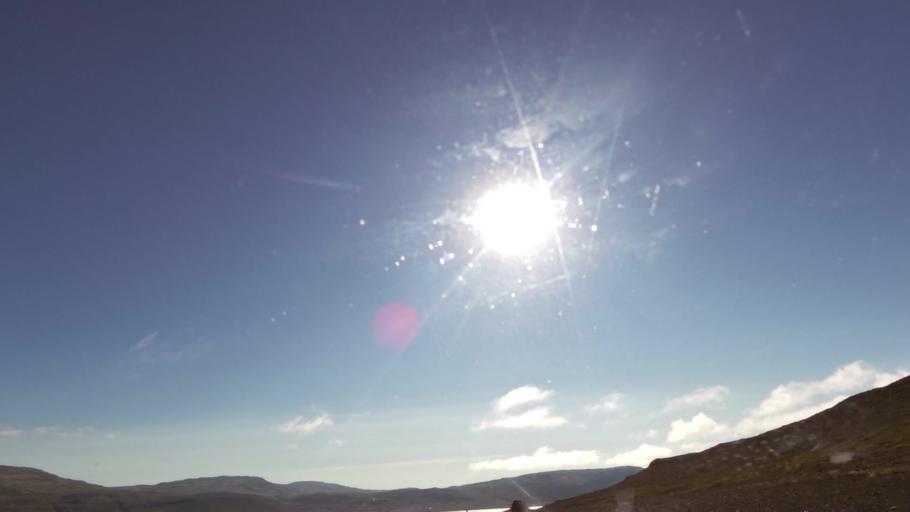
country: IS
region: West
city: Olafsvik
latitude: 65.5385
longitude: -23.8427
